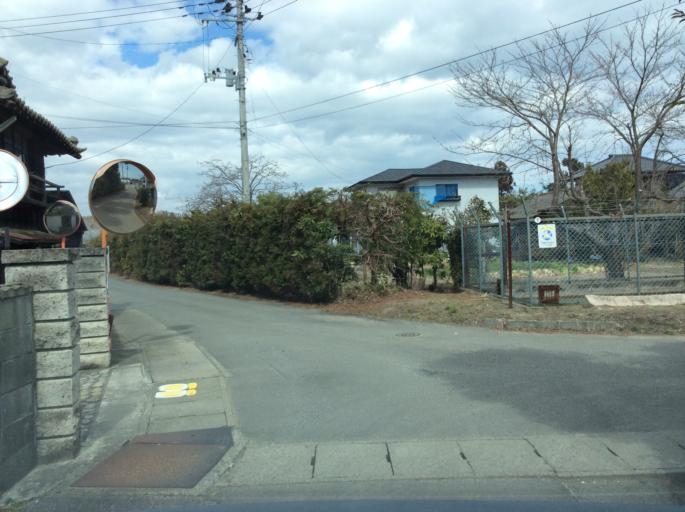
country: JP
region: Fukushima
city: Iwaki
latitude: 37.0831
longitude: 140.9492
